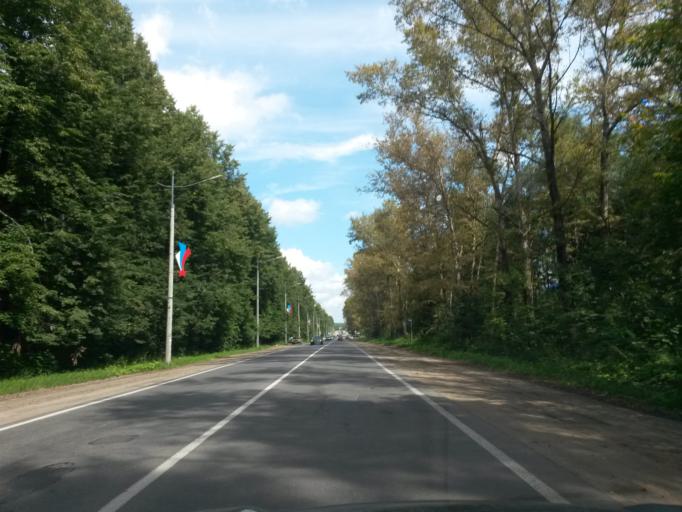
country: RU
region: Jaroslavl
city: Pereslavl'-Zalesskiy
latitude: 56.7552
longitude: 38.8653
